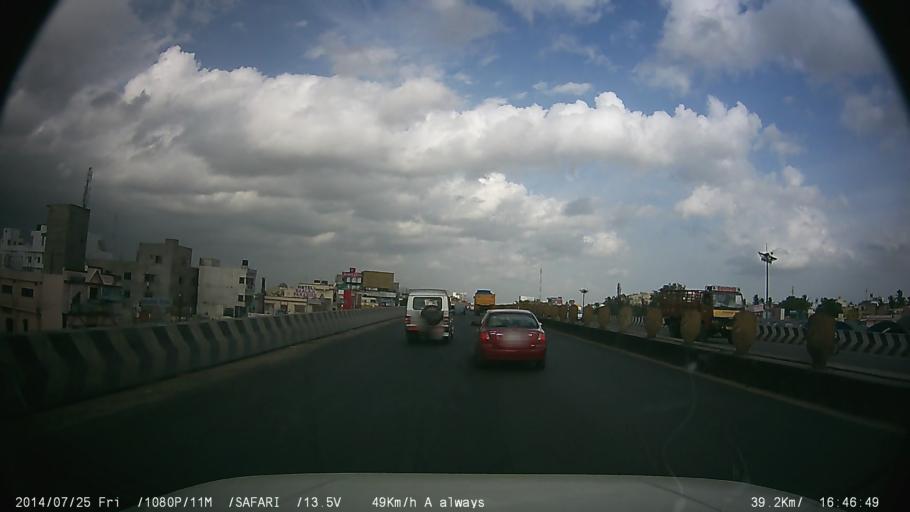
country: IN
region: Tamil Nadu
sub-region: Krishnagiri
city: Hosur
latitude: 12.7360
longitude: 77.8264
